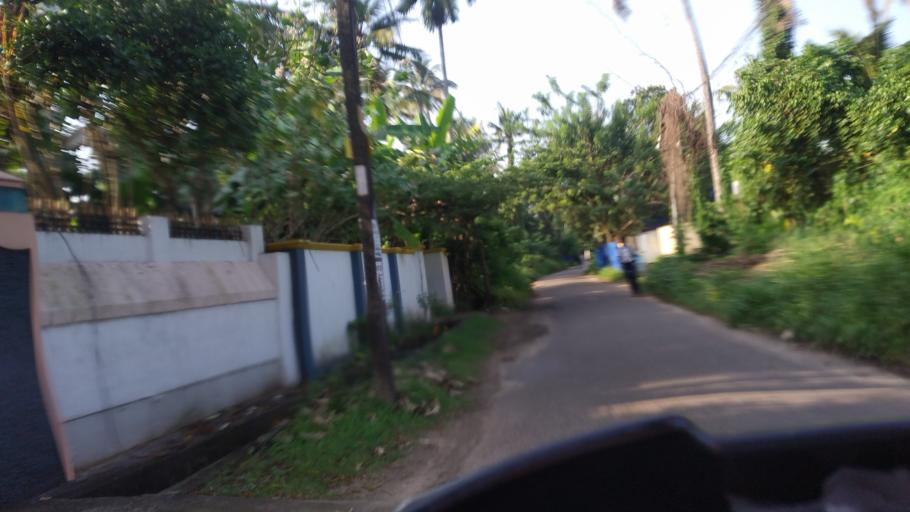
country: IN
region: Kerala
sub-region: Ernakulam
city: Elur
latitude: 10.0425
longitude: 76.2275
